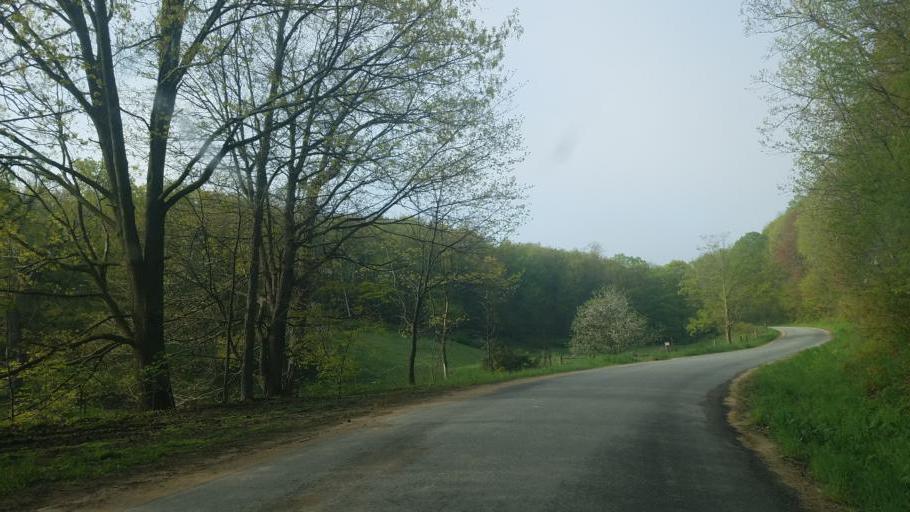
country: US
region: Wisconsin
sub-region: Vernon County
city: Hillsboro
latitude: 43.6003
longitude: -90.4054
